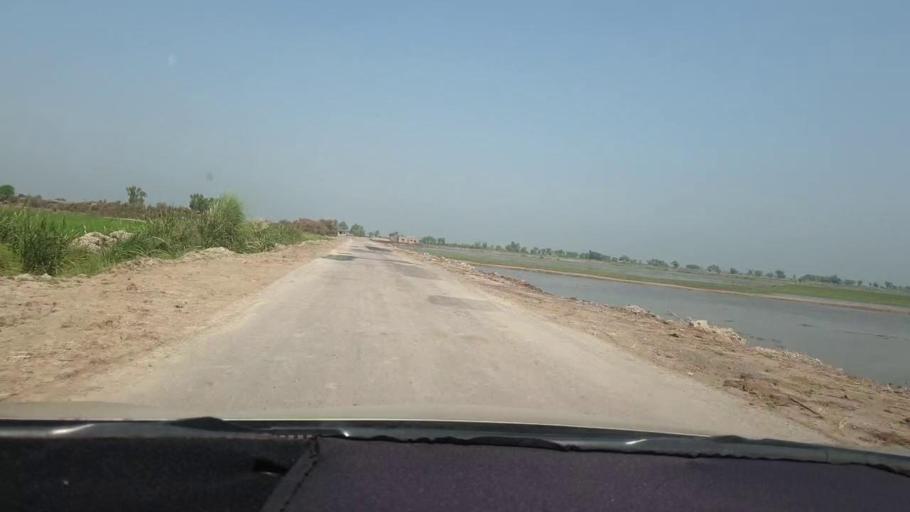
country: PK
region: Sindh
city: Miro Khan
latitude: 27.8144
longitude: 68.0284
